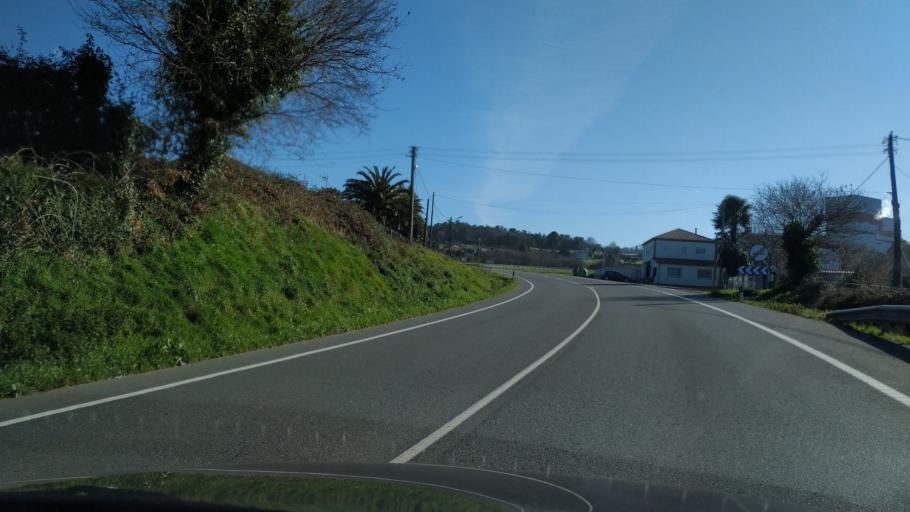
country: ES
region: Galicia
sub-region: Provincia de Pontevedra
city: Silleda
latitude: 42.7065
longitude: -8.2644
